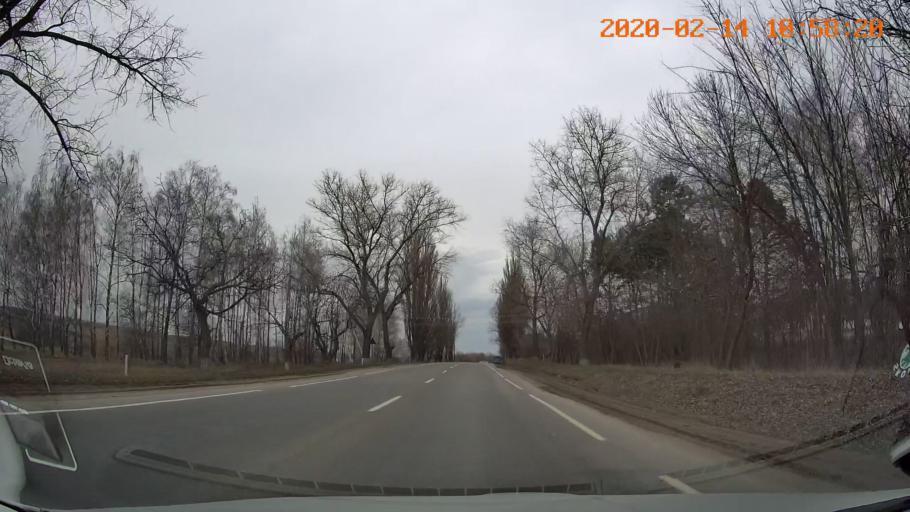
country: MD
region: Raionul Edinet
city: Edinet
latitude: 48.1302
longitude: 27.3637
